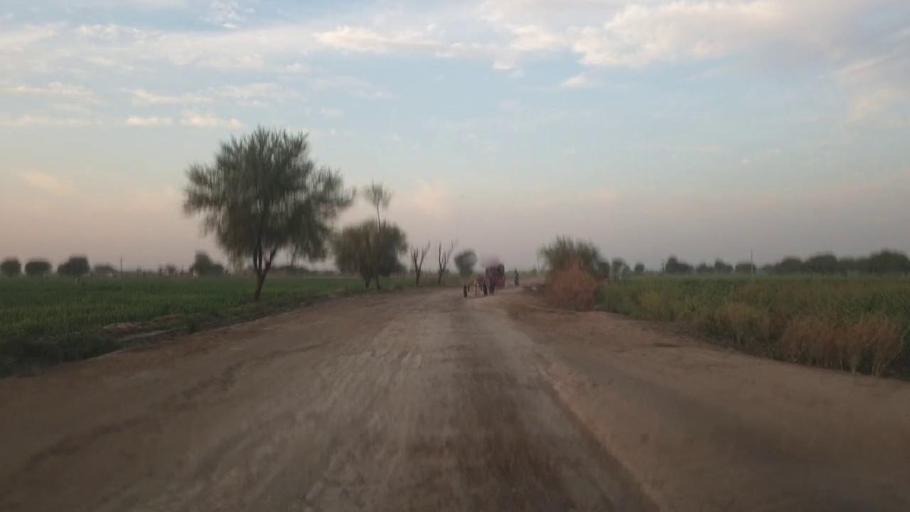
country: PK
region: Sindh
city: Umarkot
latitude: 25.2664
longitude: 69.6770
